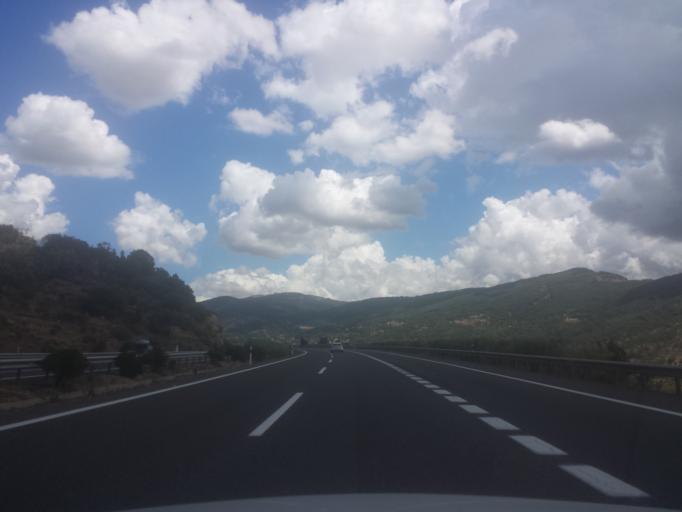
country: ES
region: Extremadura
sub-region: Provincia de Caceres
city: Hervas
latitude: 40.2952
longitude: -5.8929
